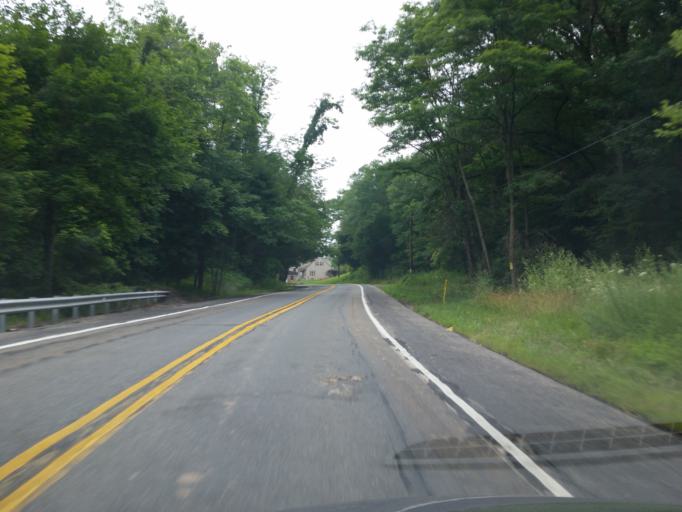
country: US
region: Pennsylvania
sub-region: Schuylkill County
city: Pine Grove
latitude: 40.5280
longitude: -76.4741
